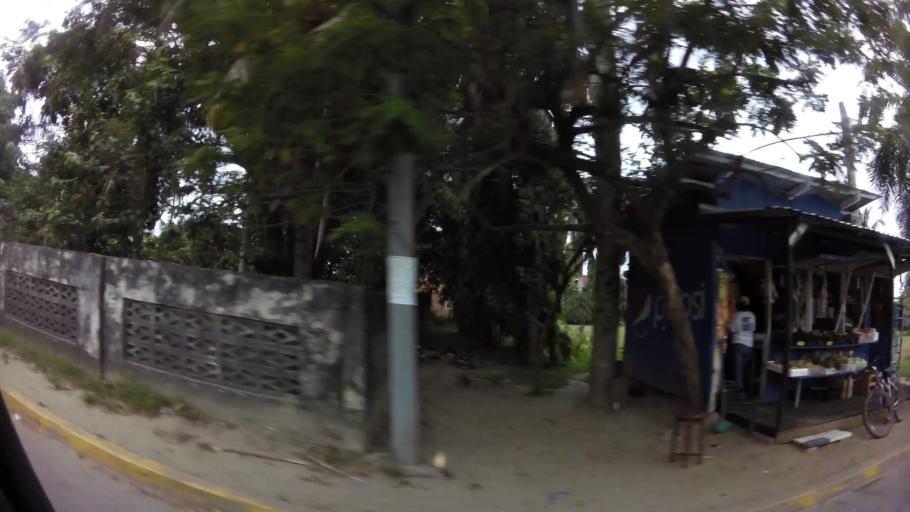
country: HN
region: Atlantida
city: Tela
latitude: 15.7637
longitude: -87.4799
